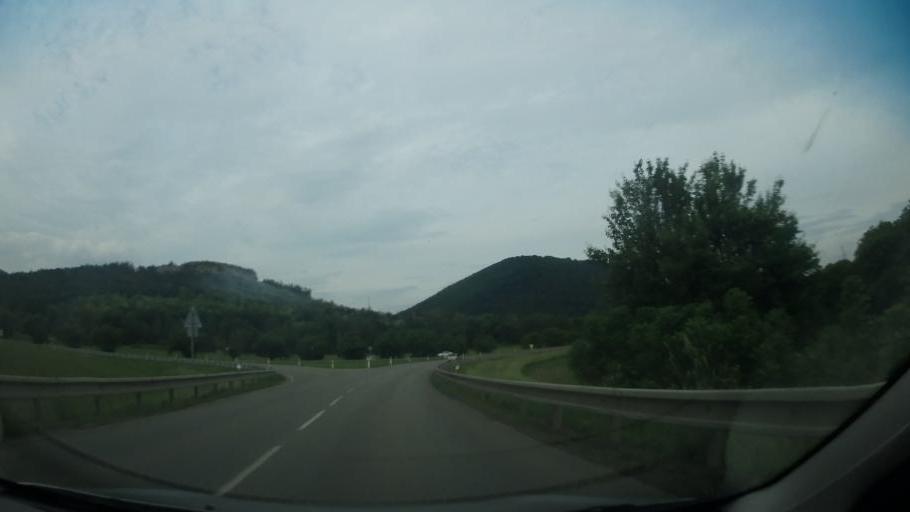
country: CZ
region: South Moravian
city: Predklasteri
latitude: 49.3603
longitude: 16.3960
